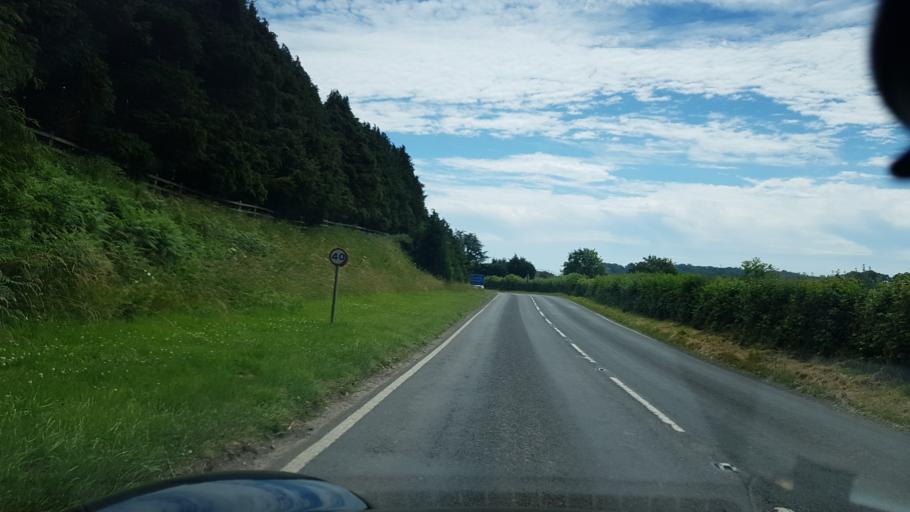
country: GB
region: Wales
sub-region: Carmarthenshire
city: Saint Clears
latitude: 51.7786
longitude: -4.4691
